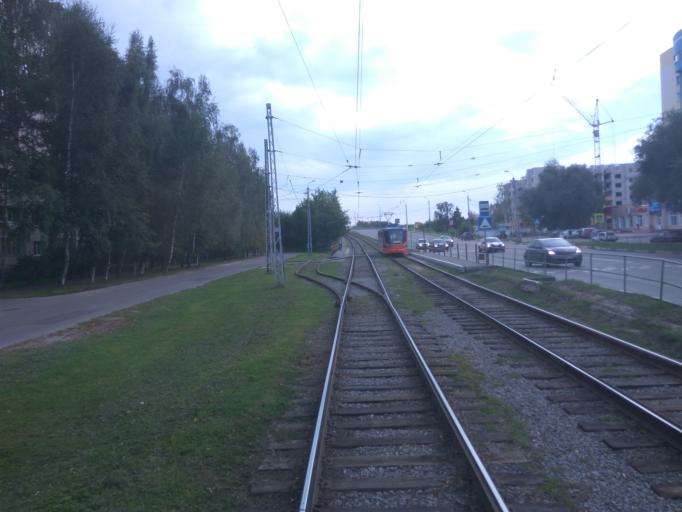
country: RU
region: Moskovskaya
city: Kolomna
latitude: 55.0753
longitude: 38.7611
